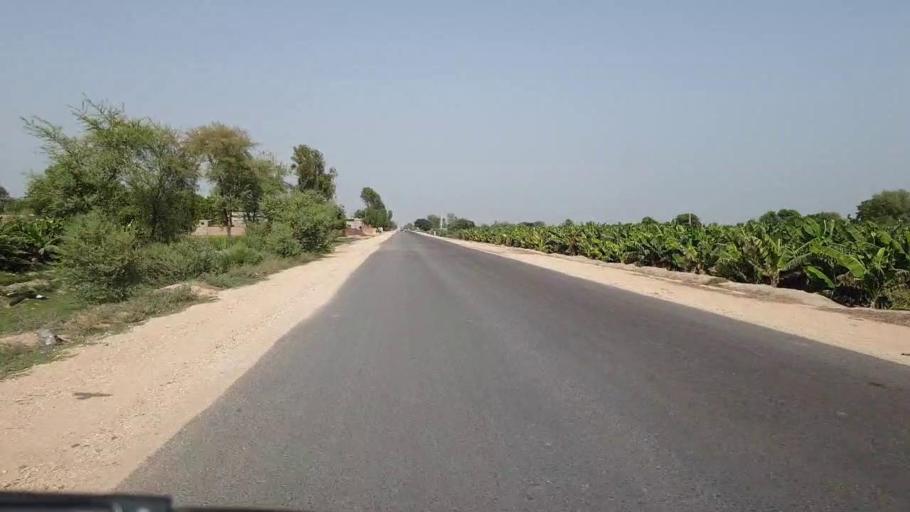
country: PK
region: Sindh
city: Sakrand
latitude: 26.2451
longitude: 68.2441
